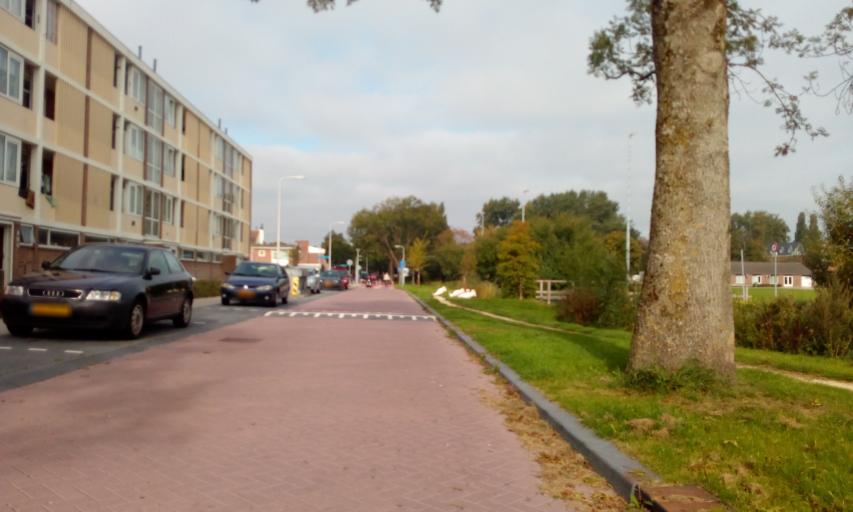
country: NL
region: South Holland
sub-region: Gemeente Voorschoten
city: Voorschoten
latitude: 52.1266
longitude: 4.4595
